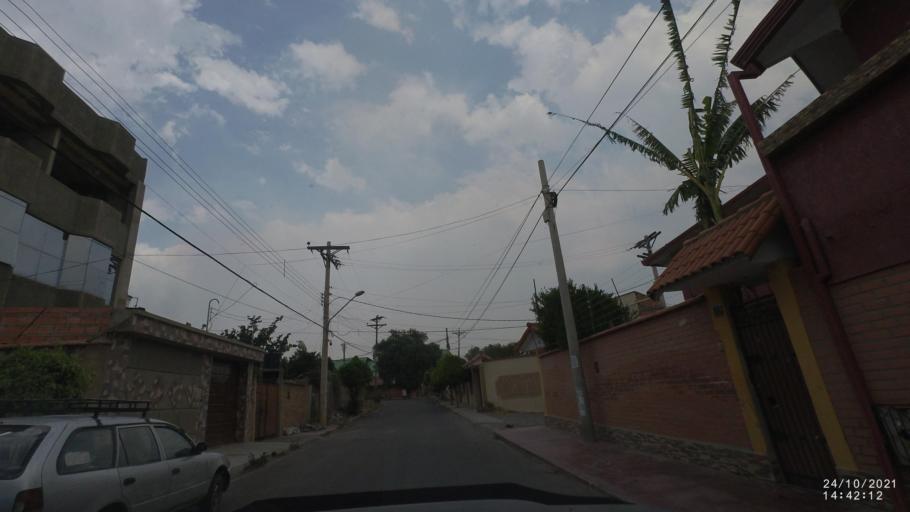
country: BO
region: Cochabamba
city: Cochabamba
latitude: -17.3529
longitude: -66.1788
